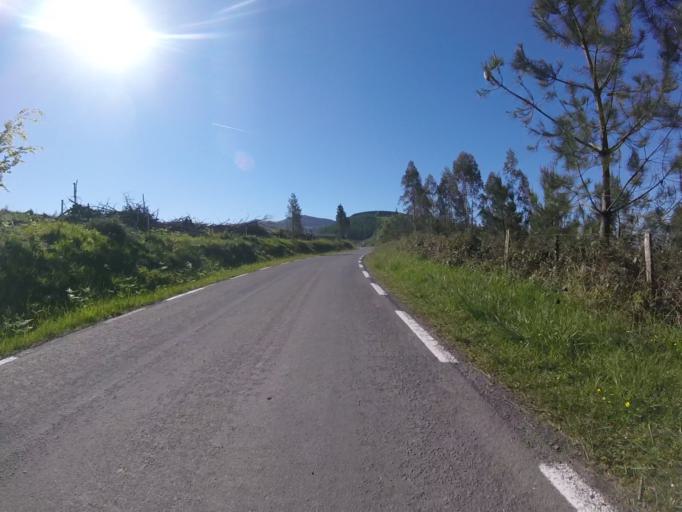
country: ES
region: Basque Country
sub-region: Provincia de Guipuzcoa
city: Errezil
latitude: 43.2068
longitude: -2.1990
